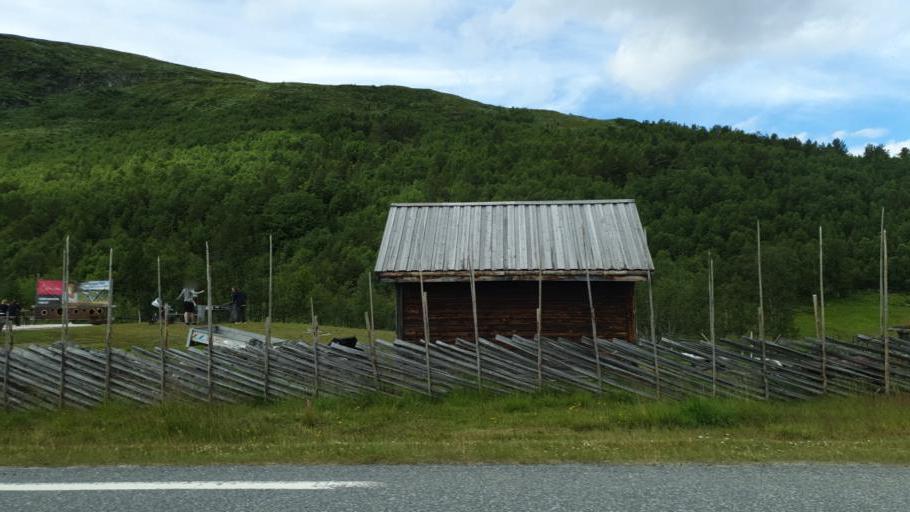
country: NO
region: Oppland
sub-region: Vaga
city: Vagamo
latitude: 61.7581
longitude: 9.0707
